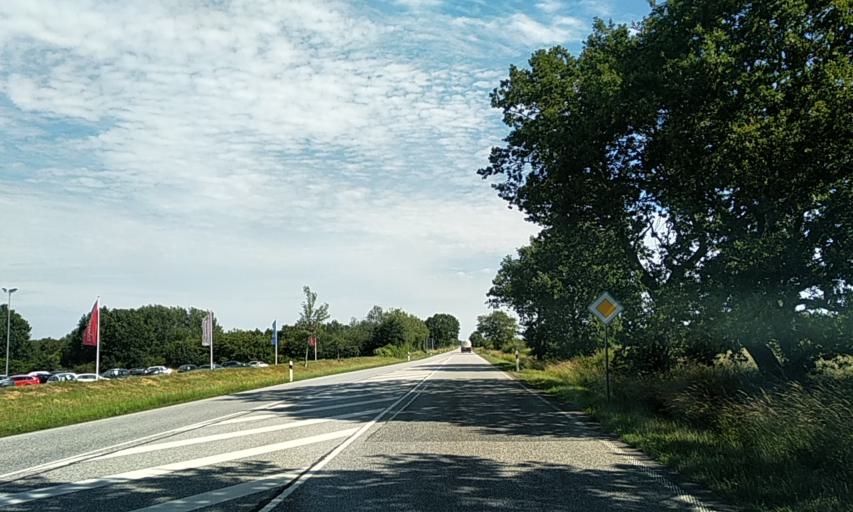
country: DE
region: Schleswig-Holstein
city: Kropp
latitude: 54.4189
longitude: 9.5300
